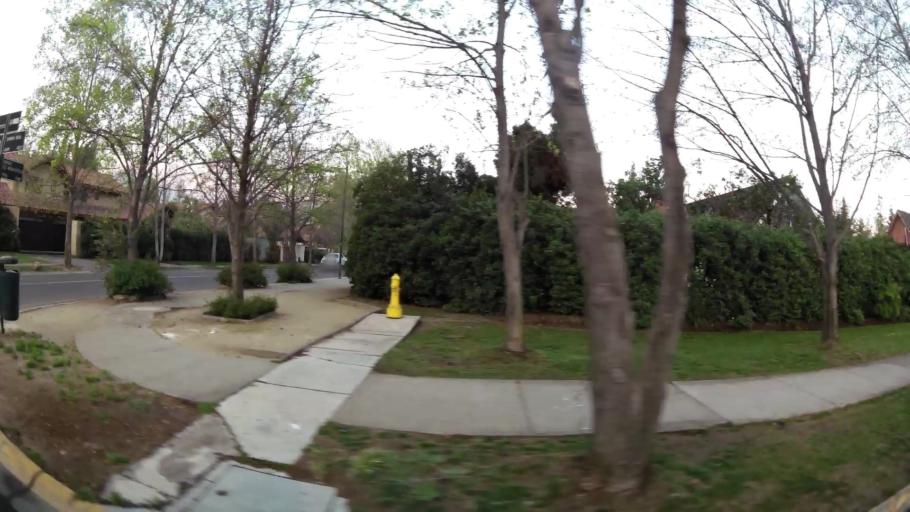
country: CL
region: Santiago Metropolitan
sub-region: Provincia de Chacabuco
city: Chicureo Abajo
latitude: -33.3345
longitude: -70.5536
